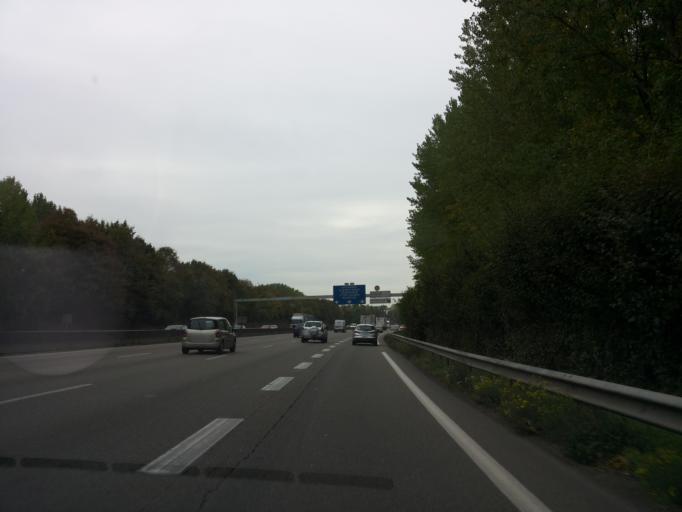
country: FR
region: Alsace
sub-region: Departement du Bas-Rhin
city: Ostwald
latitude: 48.5513
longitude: 7.7316
